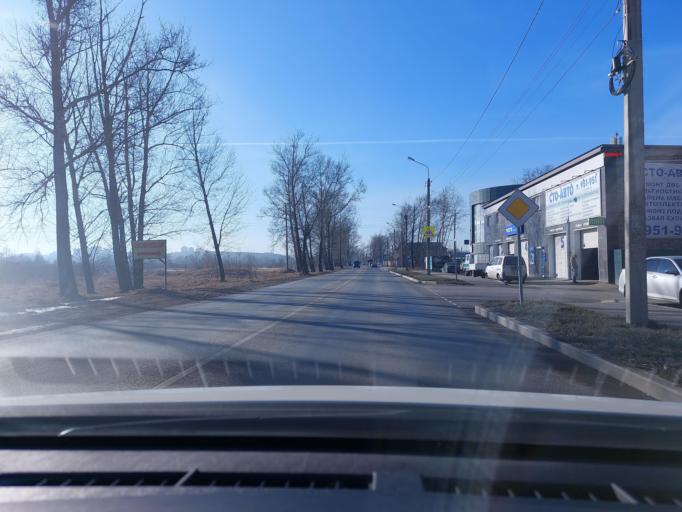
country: RU
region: Irkutsk
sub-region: Irkutskiy Rayon
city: Irkutsk
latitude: 52.3076
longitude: 104.2575
